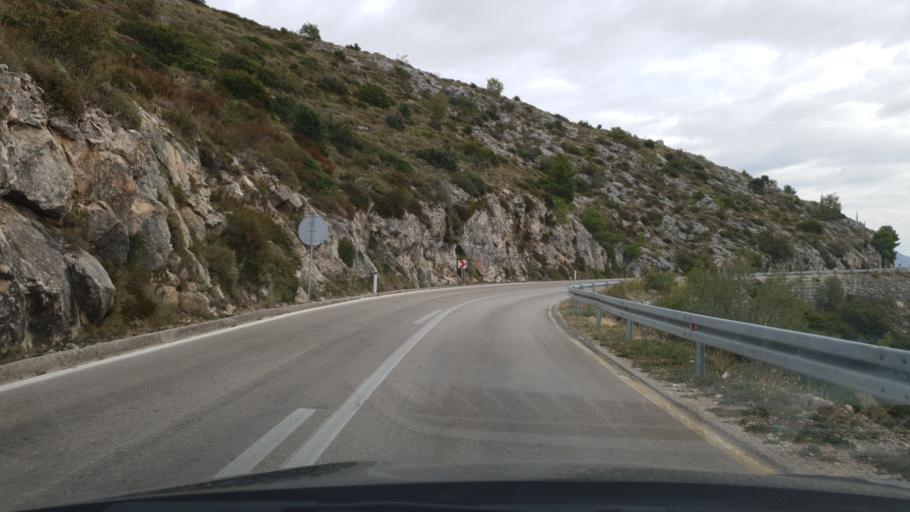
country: HR
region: Dubrovacko-Neretvanska
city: Cibaca
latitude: 42.6591
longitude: 18.1708
